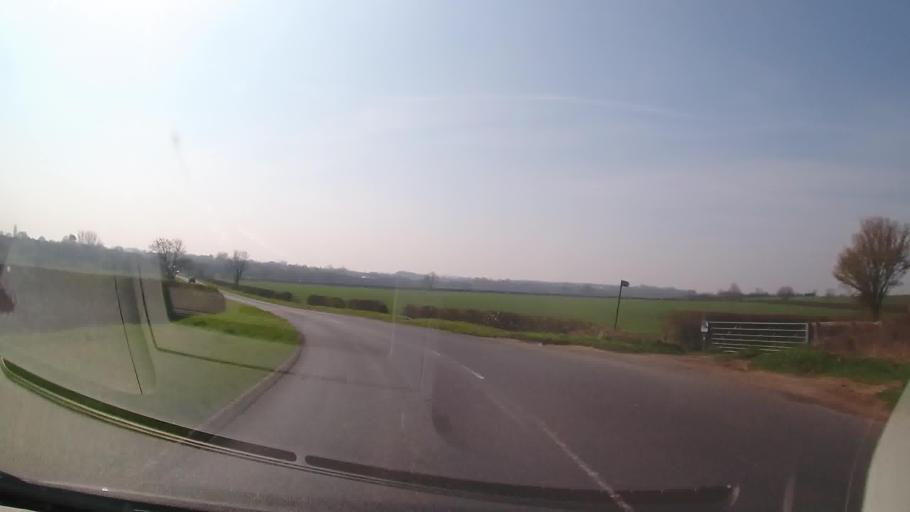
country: GB
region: England
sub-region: Leicestershire
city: Anstey
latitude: 52.6662
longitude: -1.2052
